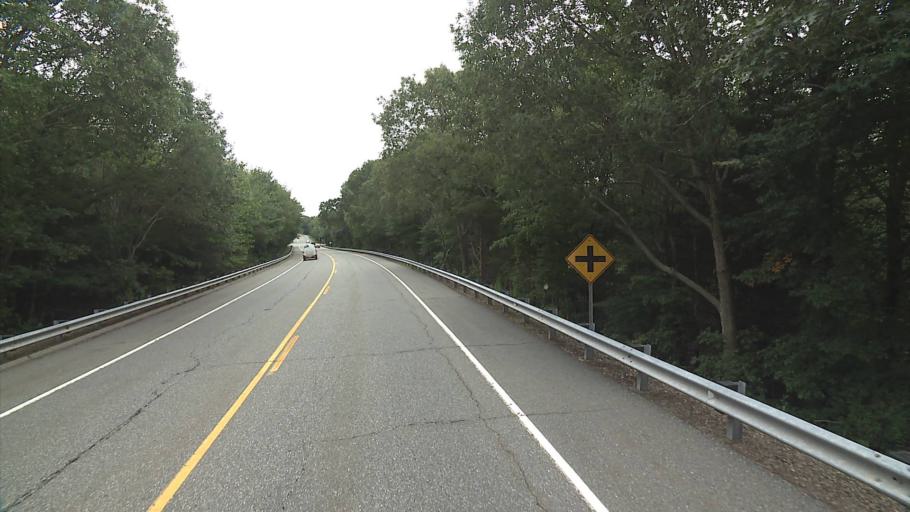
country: US
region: Connecticut
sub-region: Middlesex County
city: Old Saybrook Center
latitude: 41.3036
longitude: -72.3288
